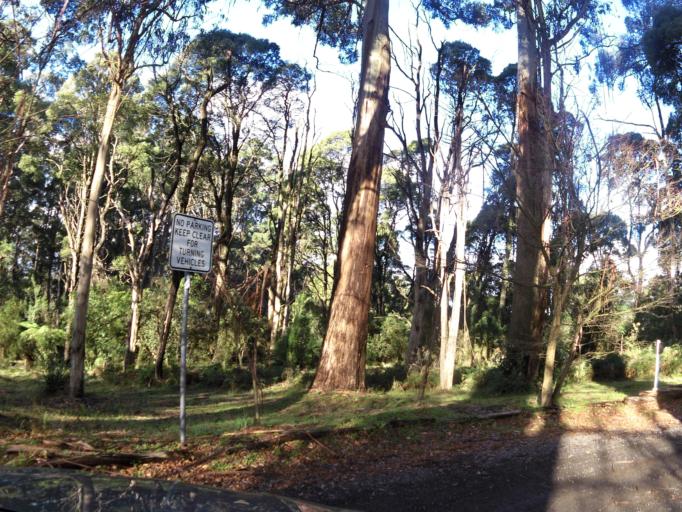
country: AU
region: Victoria
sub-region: Yarra Ranges
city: Kallista
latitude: -37.8849
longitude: 145.3624
